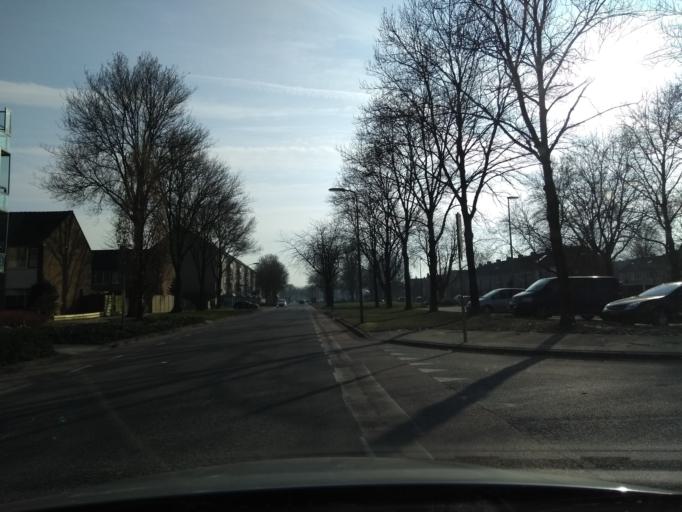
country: NL
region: Overijssel
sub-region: Gemeente Hengelo
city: Hengelo
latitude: 52.2654
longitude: 6.8245
